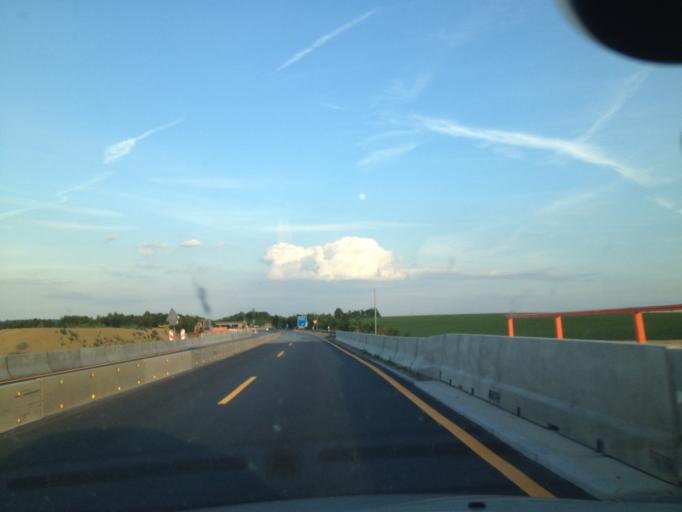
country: DE
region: Bavaria
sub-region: Regierungsbezirk Unterfranken
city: Marktbreit
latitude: 49.6535
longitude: 10.1379
